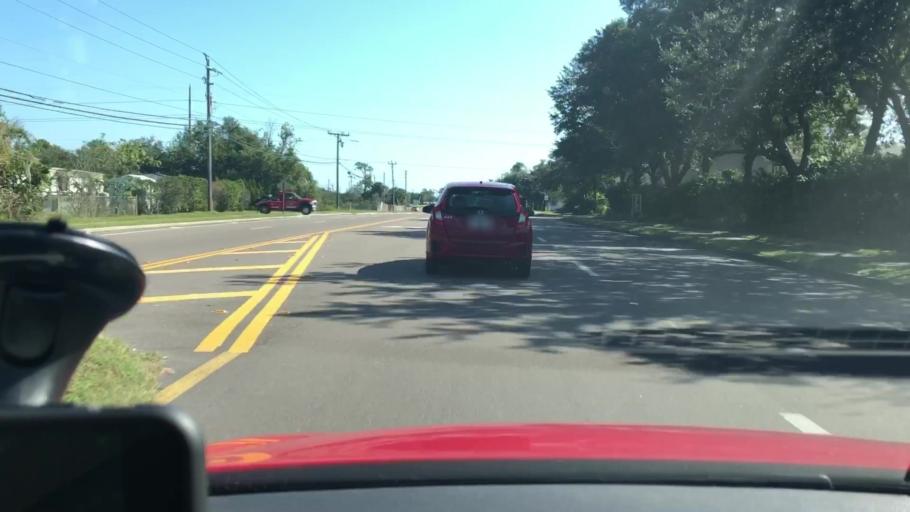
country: US
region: Florida
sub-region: Volusia County
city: Ormond Beach
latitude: 29.2617
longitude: -81.0830
